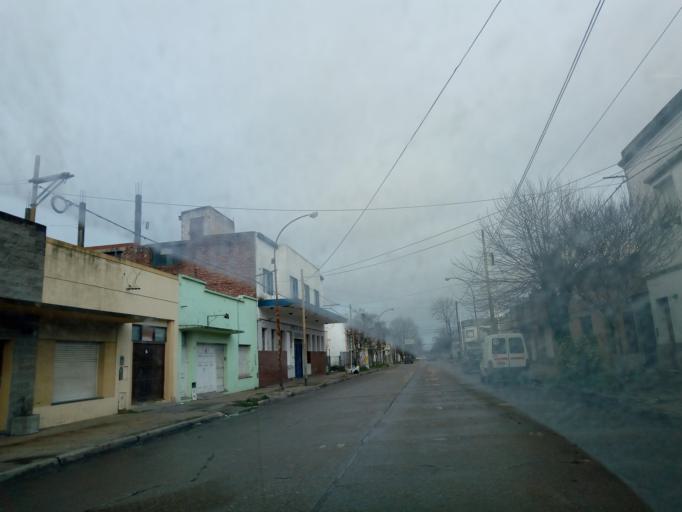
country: AR
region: Buenos Aires
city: Necochea
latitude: -38.5592
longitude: -58.7335
